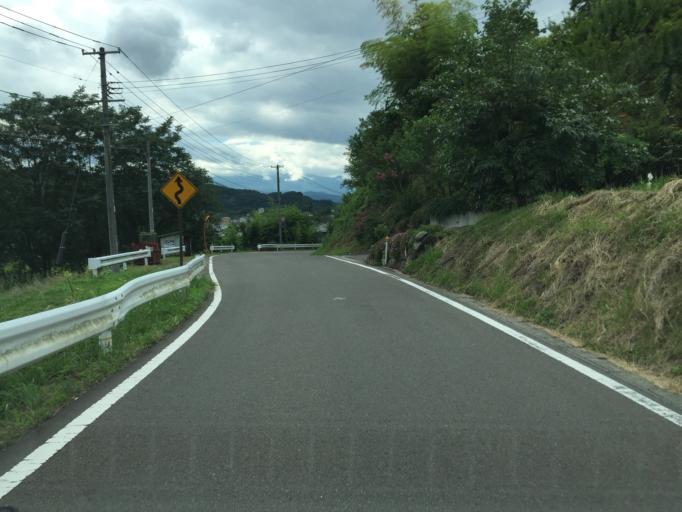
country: JP
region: Fukushima
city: Fukushima-shi
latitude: 37.7480
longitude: 140.4948
